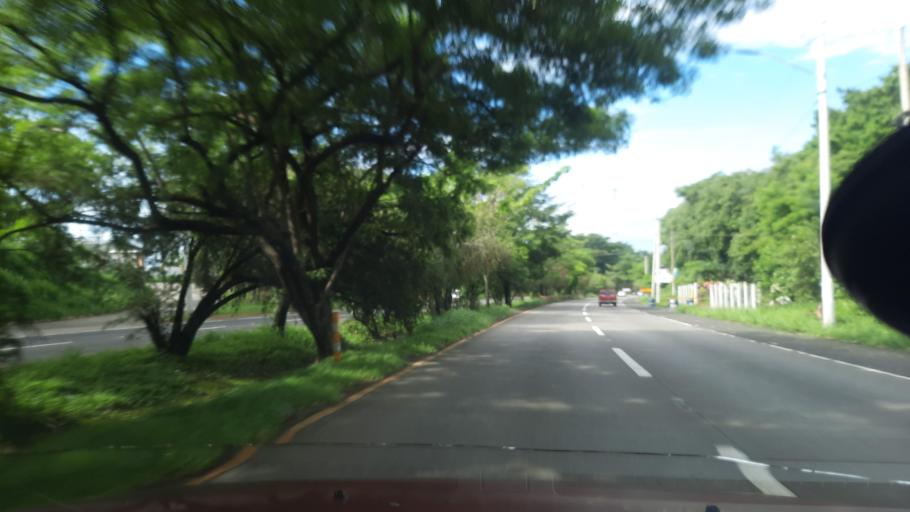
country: SV
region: La Paz
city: Olocuilta
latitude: 13.5384
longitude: -89.1111
